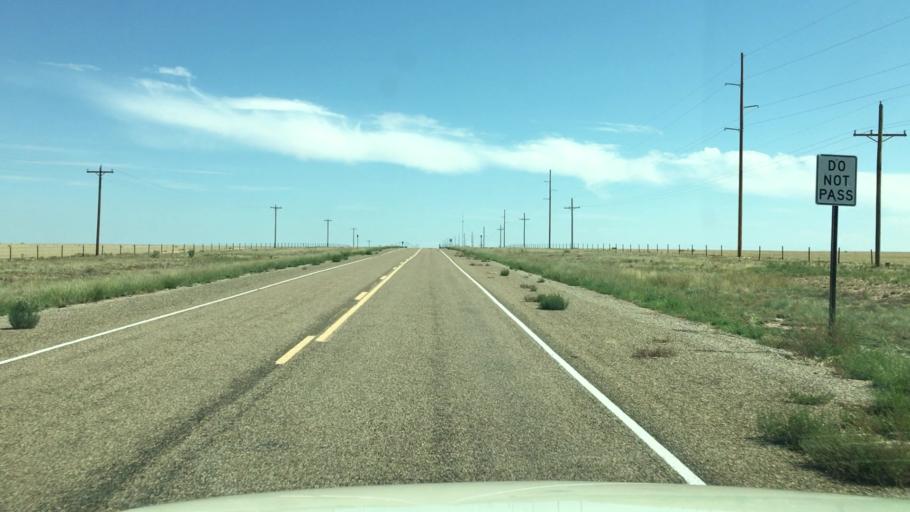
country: US
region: New Mexico
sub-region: Chaves County
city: Roswell
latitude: 33.9441
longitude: -104.5911
